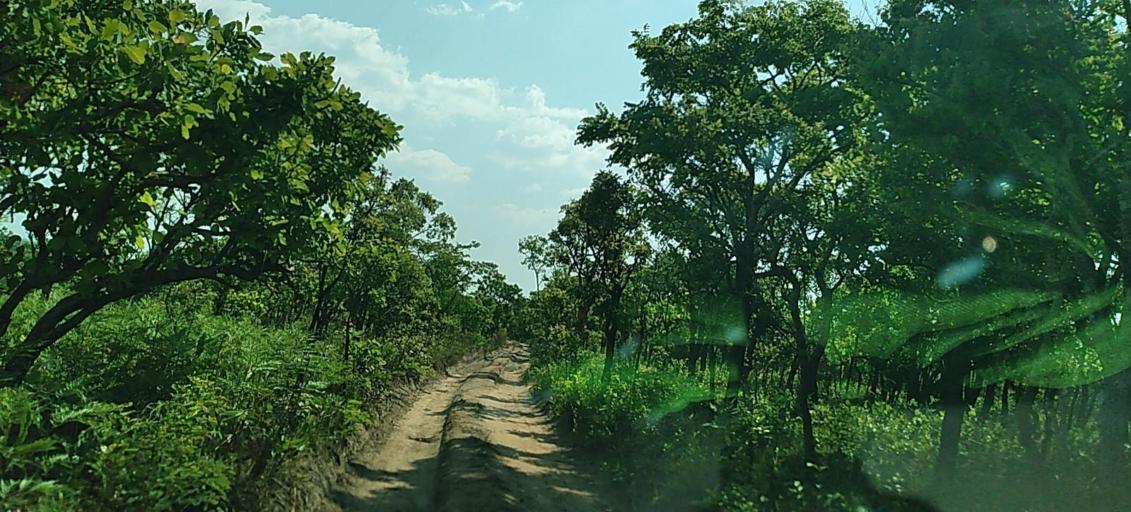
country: ZM
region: North-Western
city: Mwinilunga
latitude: -11.2709
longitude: 24.9909
